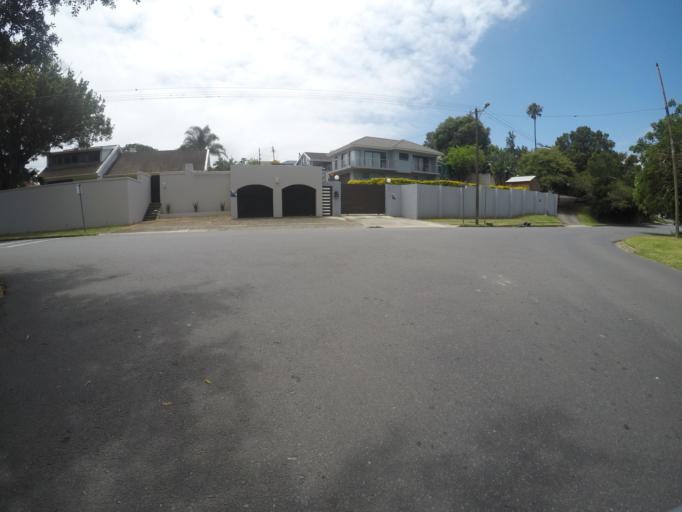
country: ZA
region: Eastern Cape
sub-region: Buffalo City Metropolitan Municipality
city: East London
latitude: -32.9902
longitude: 27.9308
